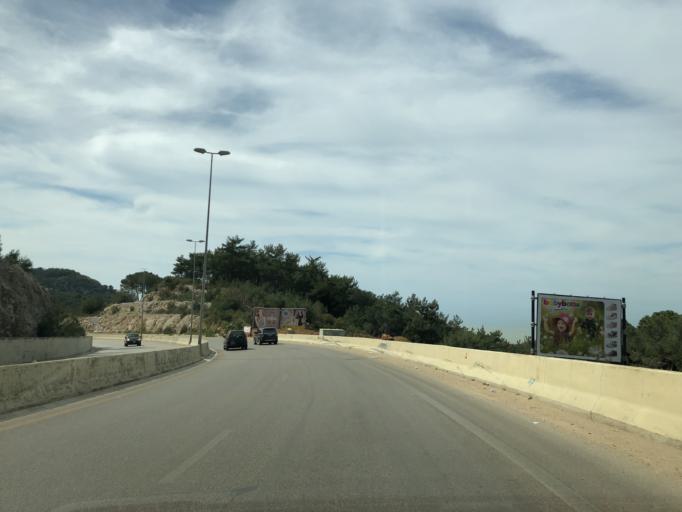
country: LB
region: Mont-Liban
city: Jdaidet el Matn
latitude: 33.9008
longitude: 35.6428
